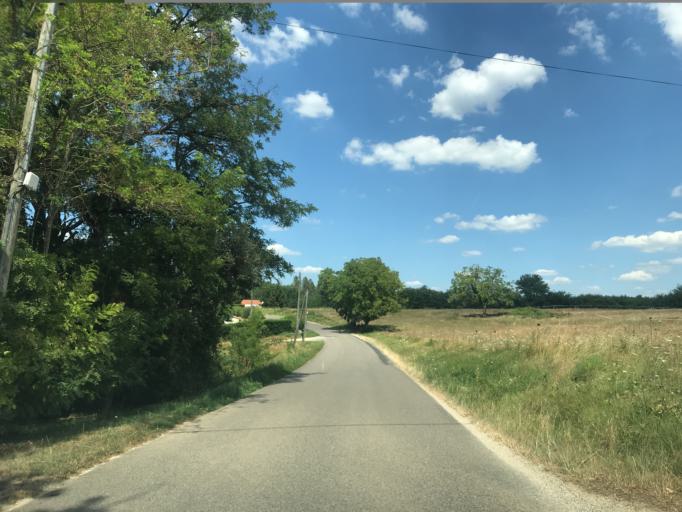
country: FR
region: Aquitaine
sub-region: Departement de la Dordogne
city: Sarlat-la-Caneda
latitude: 44.8541
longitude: 1.2053
